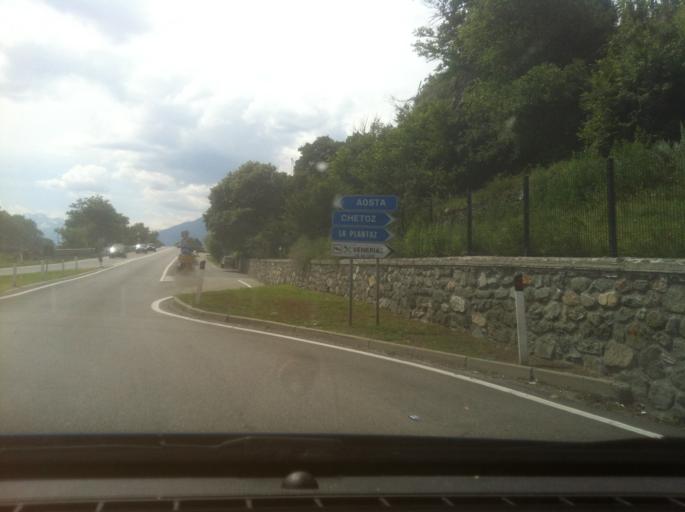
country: IT
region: Aosta Valley
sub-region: Valle d'Aosta
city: Saint Marcel
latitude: 45.7400
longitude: 7.4389
